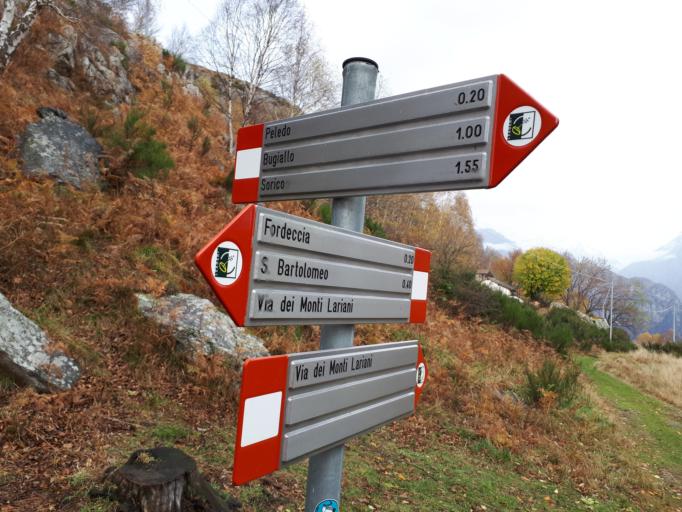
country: IT
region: Lombardy
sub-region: Provincia di Como
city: Sorico
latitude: 46.1953
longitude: 9.4015
